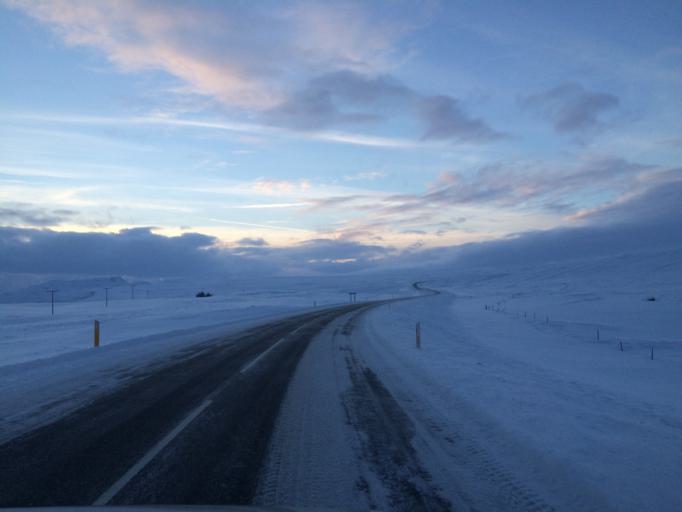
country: IS
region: South
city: Hveragerdi
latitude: 64.2304
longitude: -21.1990
